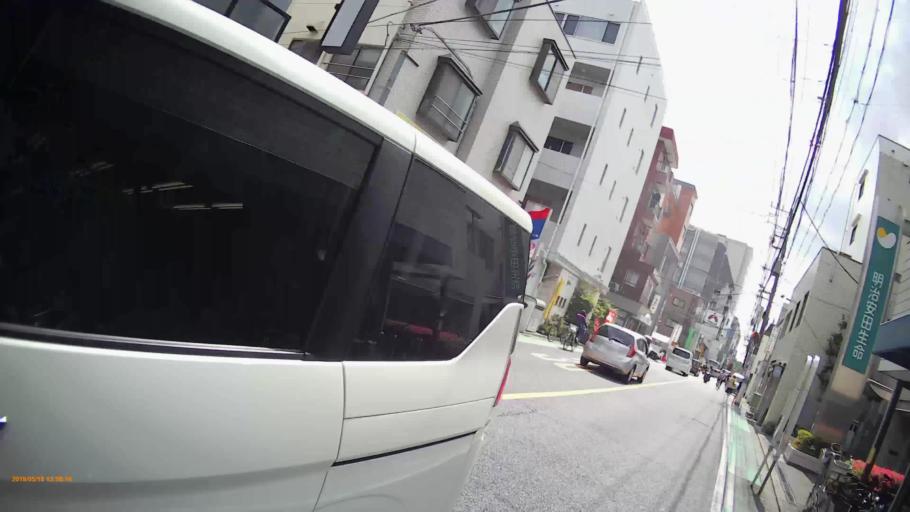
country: JP
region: Tokyo
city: Mitaka-shi
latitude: 35.6691
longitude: 139.6021
